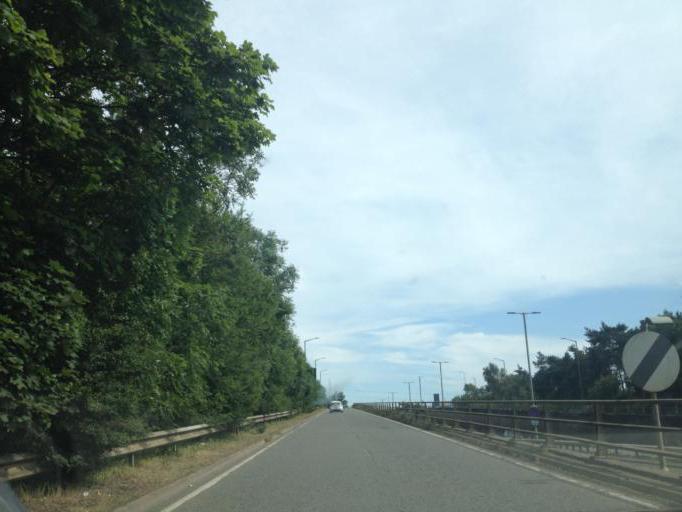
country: GB
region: England
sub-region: Hertfordshire
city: Watford
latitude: 51.6728
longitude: -0.3732
